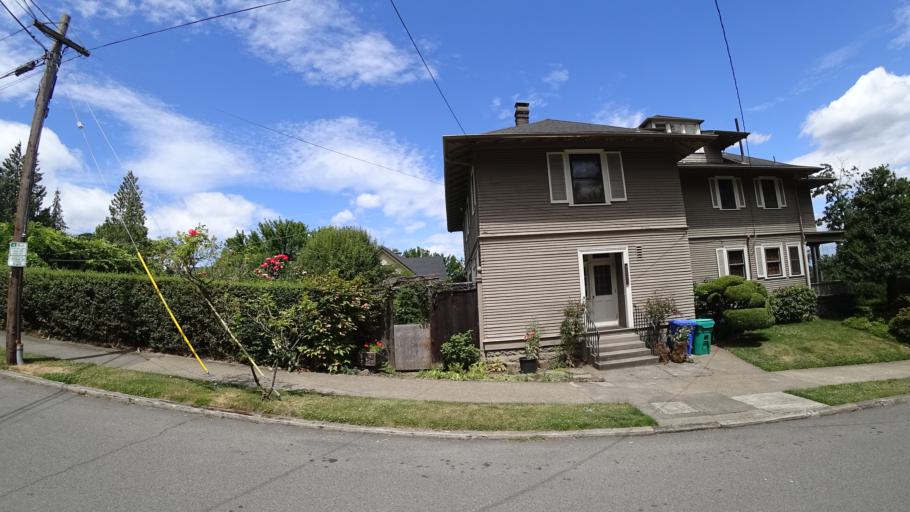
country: US
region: Oregon
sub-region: Multnomah County
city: Portland
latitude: 45.5283
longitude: -122.7044
